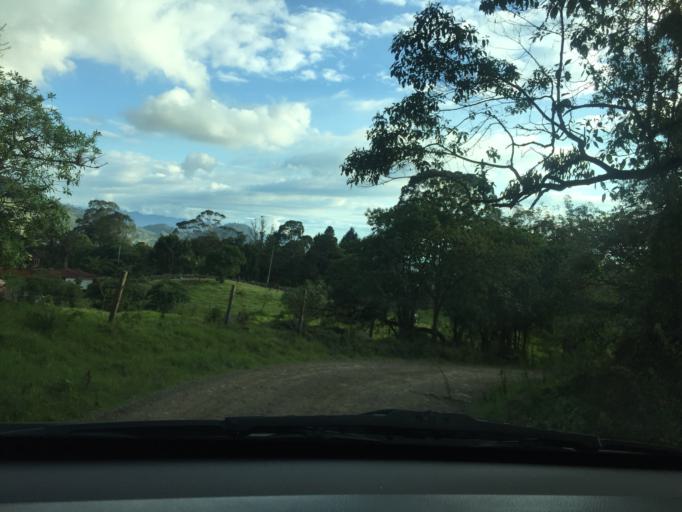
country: CO
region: Cundinamarca
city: Zipacon
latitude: 4.7418
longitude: -74.3887
